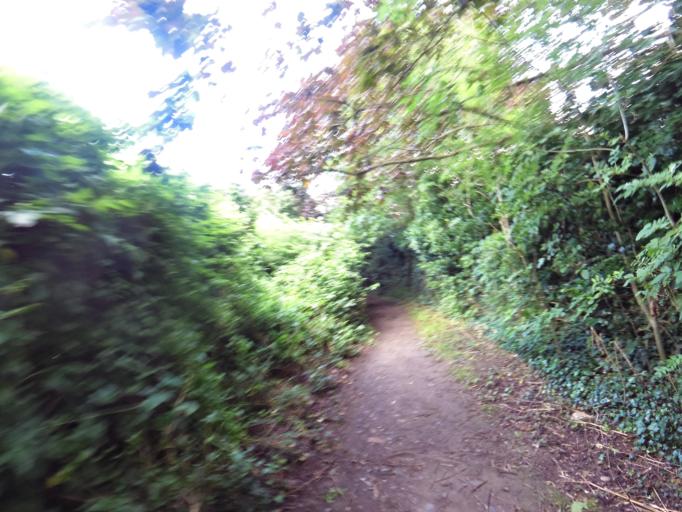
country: GB
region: England
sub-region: Suffolk
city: Ipswich
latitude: 52.0753
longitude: 1.1556
